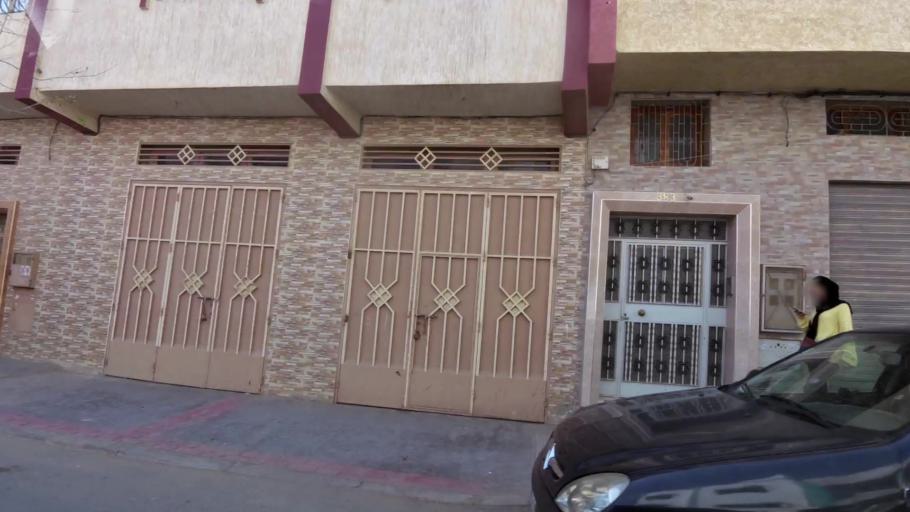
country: MA
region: Tanger-Tetouan
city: Tetouan
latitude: 35.5882
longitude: -5.3587
